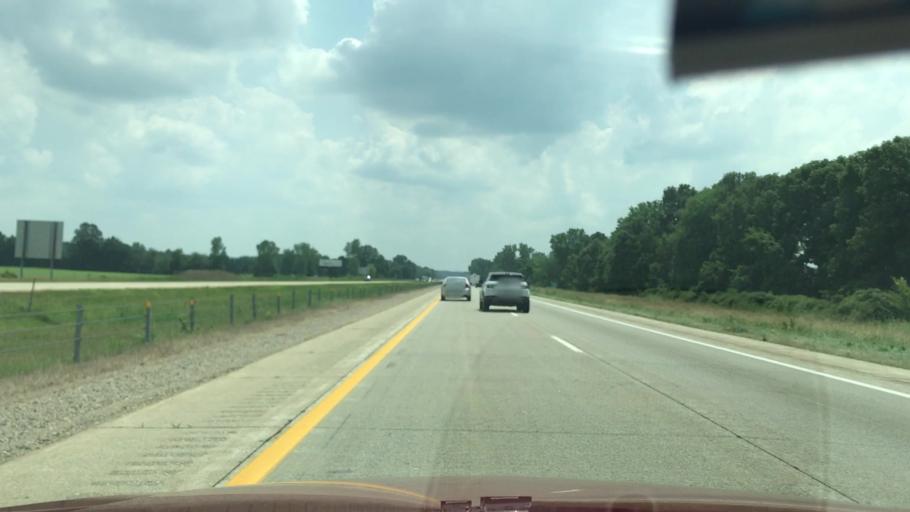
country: US
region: Michigan
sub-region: Allegan County
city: Plainwell
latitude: 42.4288
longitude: -85.6609
